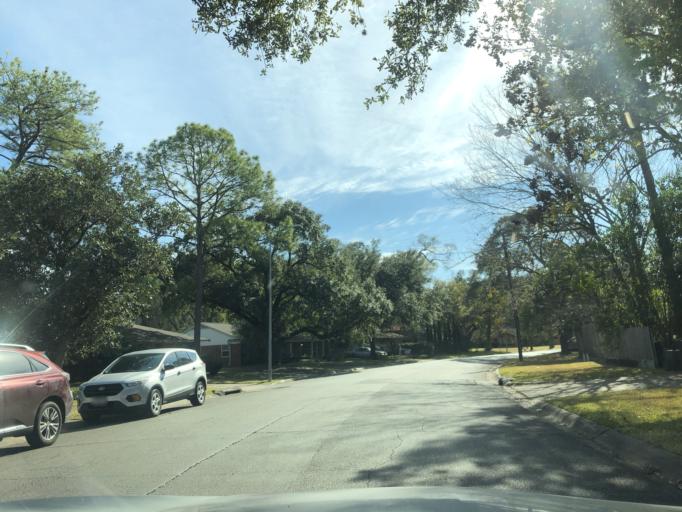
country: US
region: Texas
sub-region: Harris County
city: Bellaire
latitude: 29.6776
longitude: -95.5144
